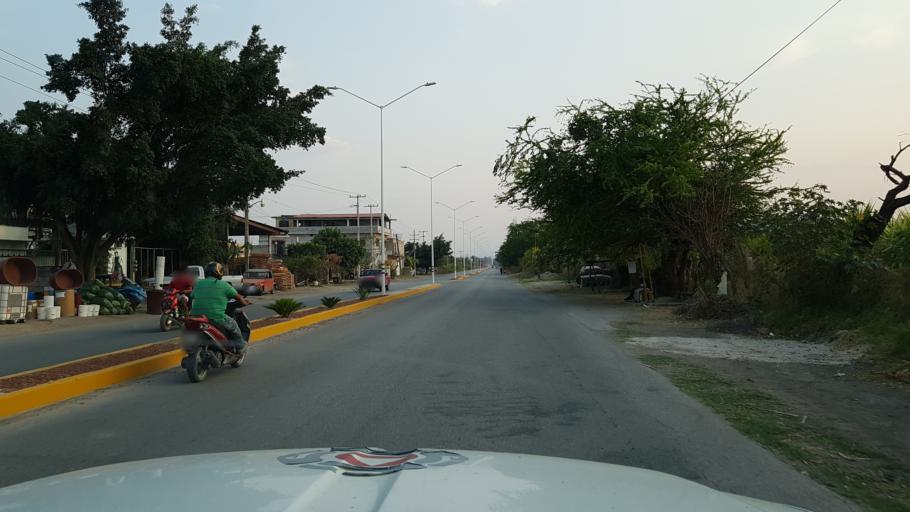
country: MX
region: Morelos
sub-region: Ayala
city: Abelardo L. Rodriguez
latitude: 18.7366
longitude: -98.9878
